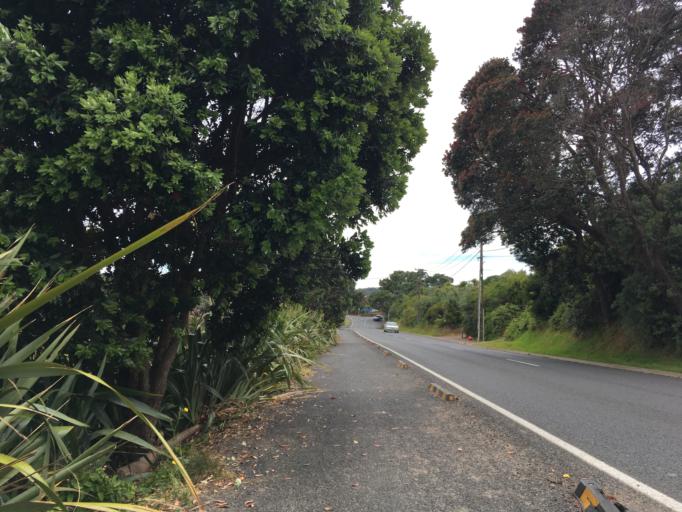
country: NZ
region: Auckland
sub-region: Auckland
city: Pakuranga
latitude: -36.7968
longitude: 175.0425
